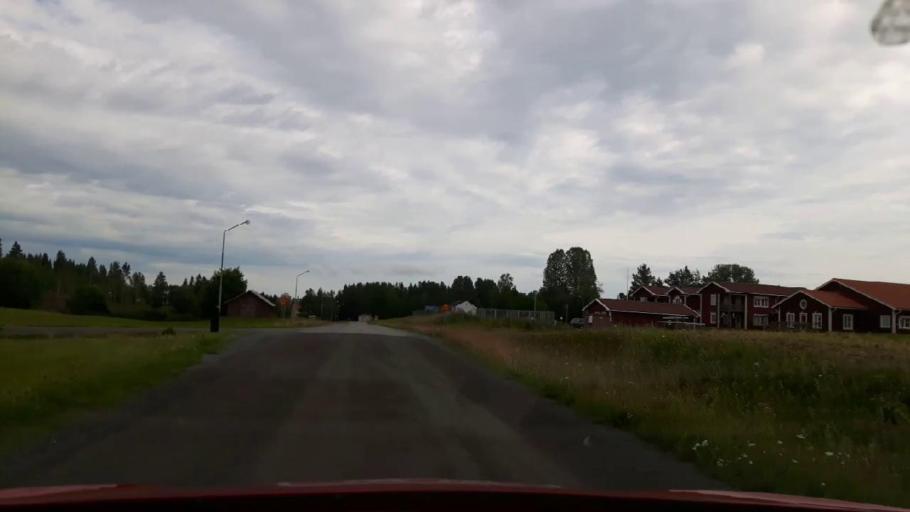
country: SE
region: Jaemtland
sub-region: OEstersunds Kommun
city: Lit
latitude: 63.4145
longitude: 15.2465
